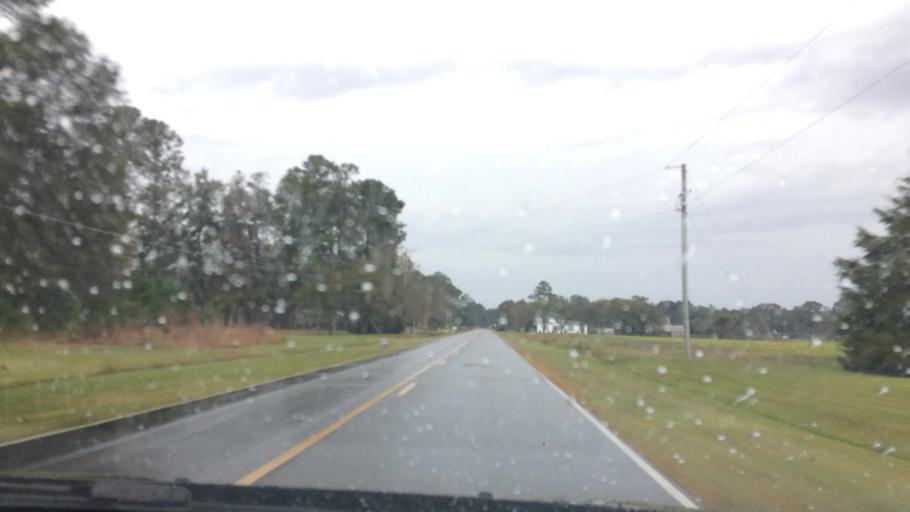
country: US
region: North Carolina
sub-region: Pitt County
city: Grifton
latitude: 35.3910
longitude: -77.4009
